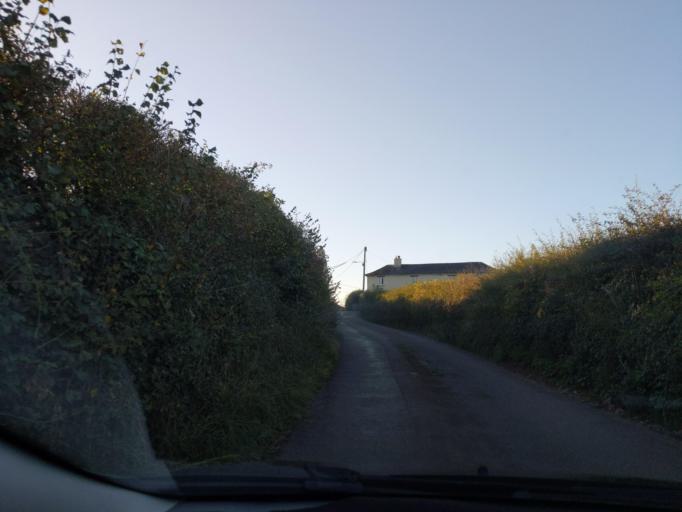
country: GB
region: England
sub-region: Plymouth
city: Plymstock
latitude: 50.3429
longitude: -4.0923
